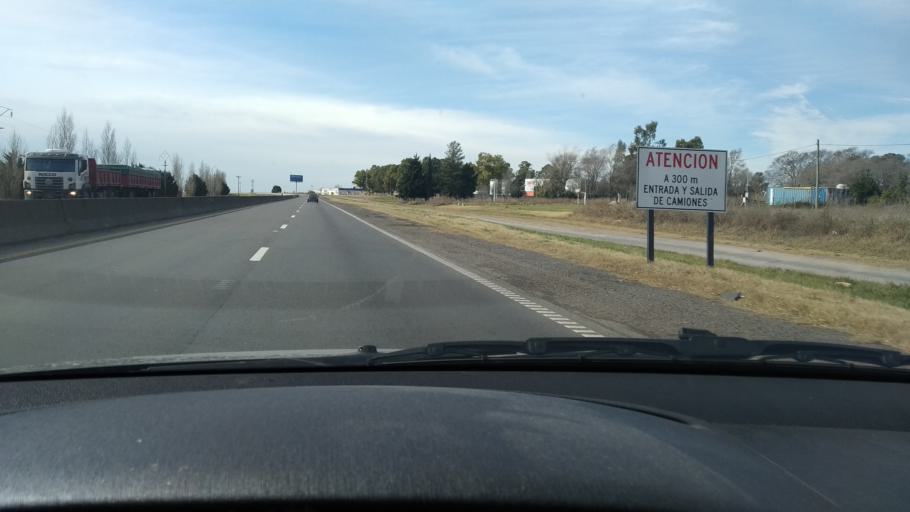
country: AR
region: Buenos Aires
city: Olavarria
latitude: -36.8998
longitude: -60.1743
